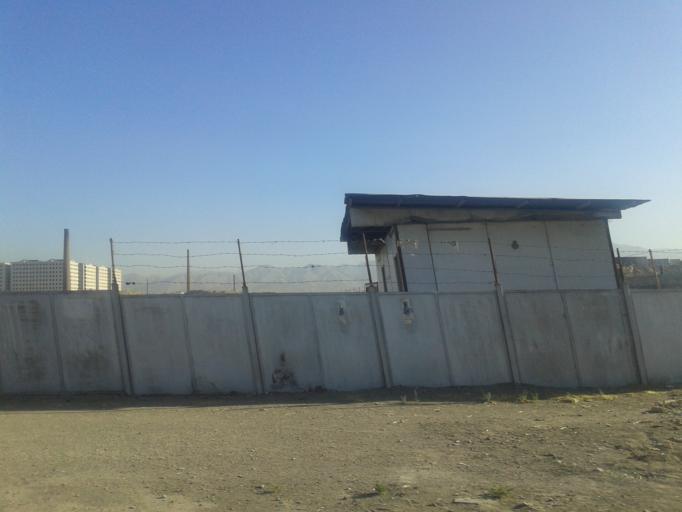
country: IR
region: Tehran
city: Rey
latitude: 35.6151
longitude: 51.3480
